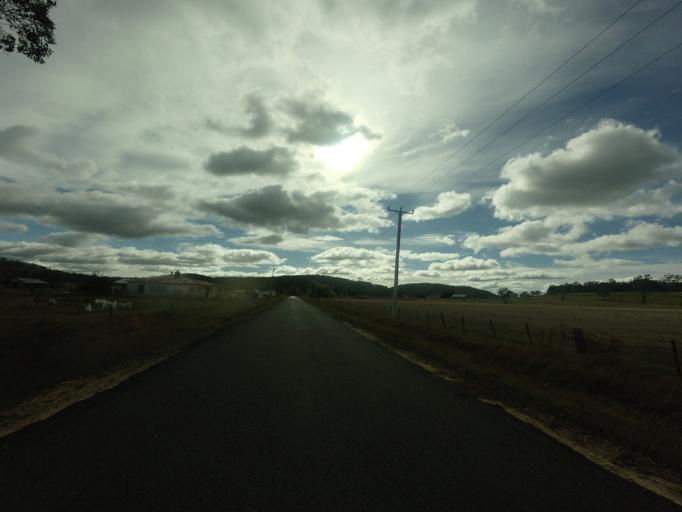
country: AU
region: Tasmania
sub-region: Brighton
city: Bridgewater
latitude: -42.4040
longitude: 147.3925
